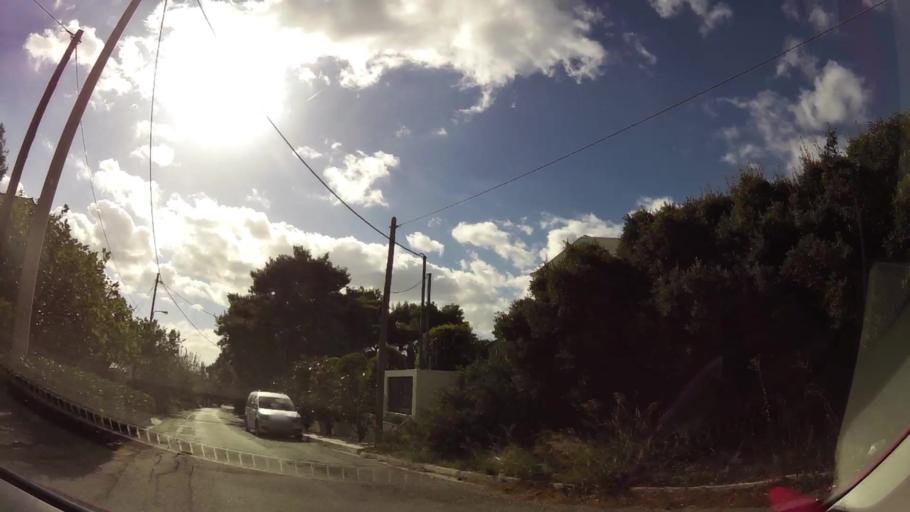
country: GR
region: Attica
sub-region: Nomarchia Anatolikis Attikis
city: Thrakomakedones
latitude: 38.1393
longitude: 23.7508
